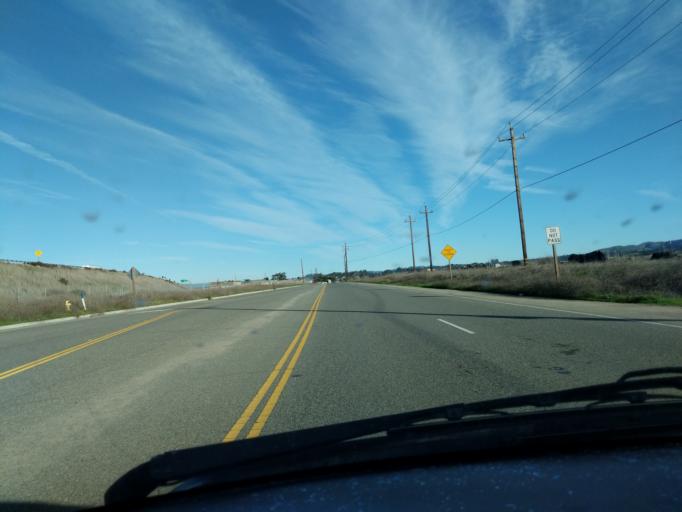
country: US
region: California
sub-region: Monterey County
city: Boronda
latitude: 36.7355
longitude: -121.6562
